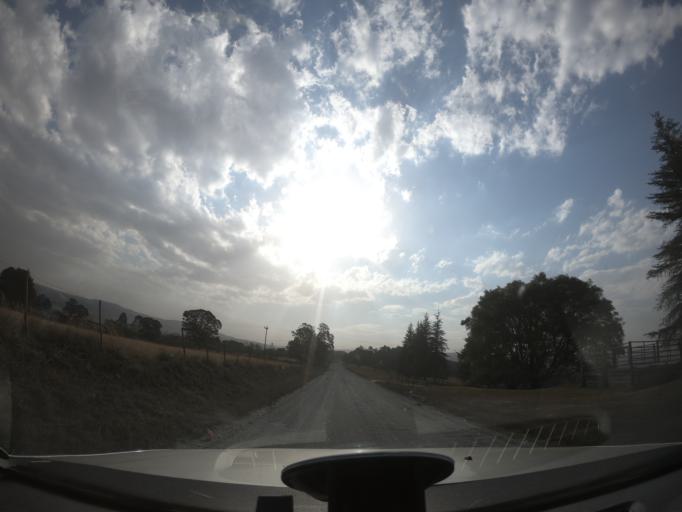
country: ZA
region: KwaZulu-Natal
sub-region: uMgungundlovu District Municipality
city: Howick
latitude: -29.4346
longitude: 30.1130
